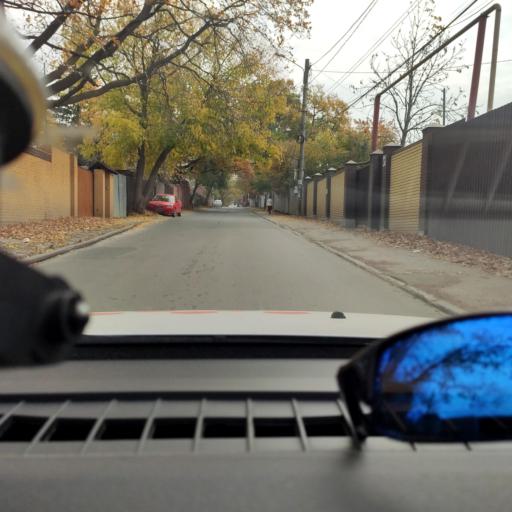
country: RU
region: Samara
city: Samara
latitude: 53.2551
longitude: 50.1938
